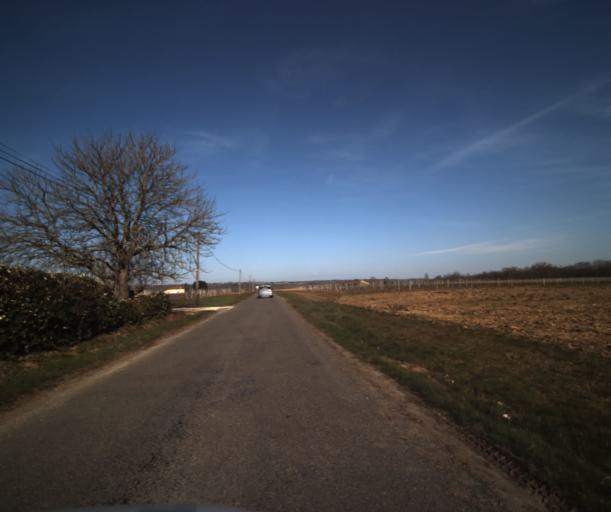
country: FR
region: Midi-Pyrenees
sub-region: Departement du Tarn-et-Garonne
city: Labastide-Saint-Pierre
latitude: 43.9219
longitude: 1.3492
